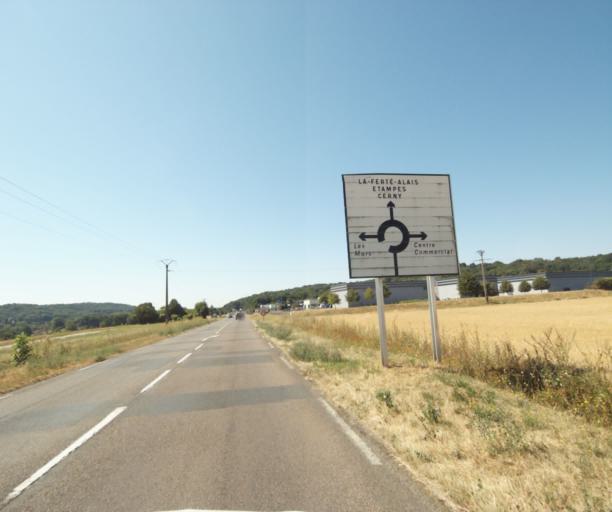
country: FR
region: Ile-de-France
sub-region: Departement de l'Essonne
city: Baulne
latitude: 48.5019
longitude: 2.3527
